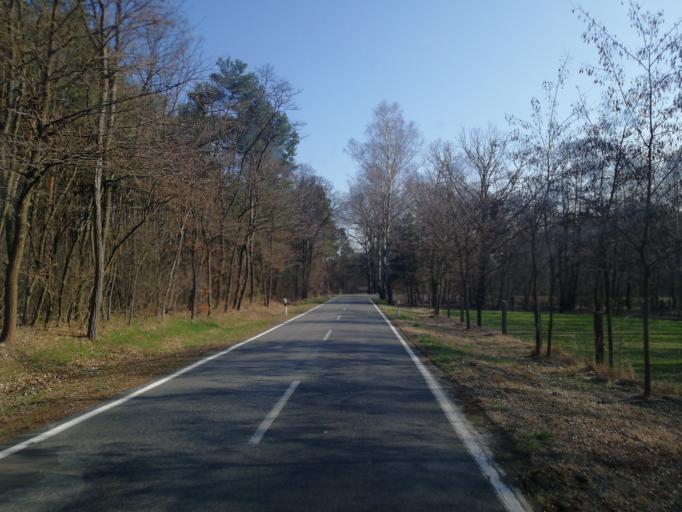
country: DE
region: Brandenburg
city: Sonnewalde
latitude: 51.7578
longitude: 13.6767
